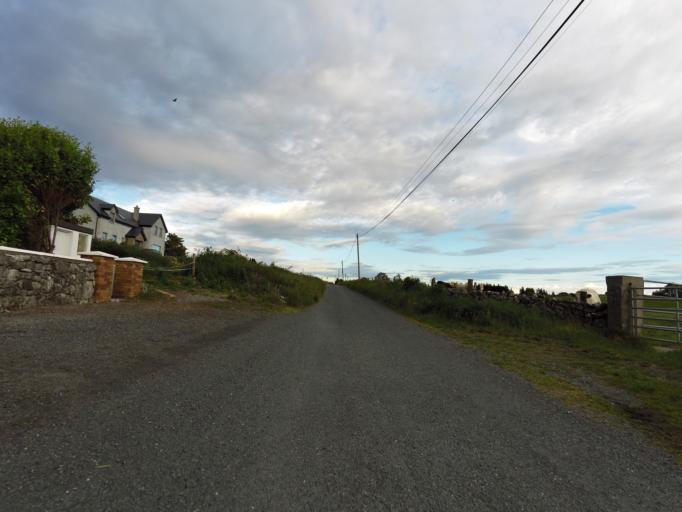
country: IE
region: Connaught
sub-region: County Galway
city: Athenry
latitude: 53.2926
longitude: -8.7211
